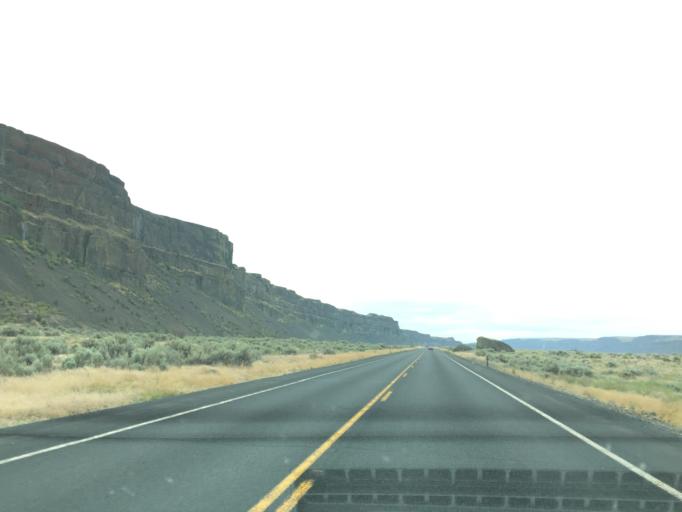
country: US
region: Washington
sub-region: Okanogan County
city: Coulee Dam
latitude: 47.7878
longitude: -119.1940
